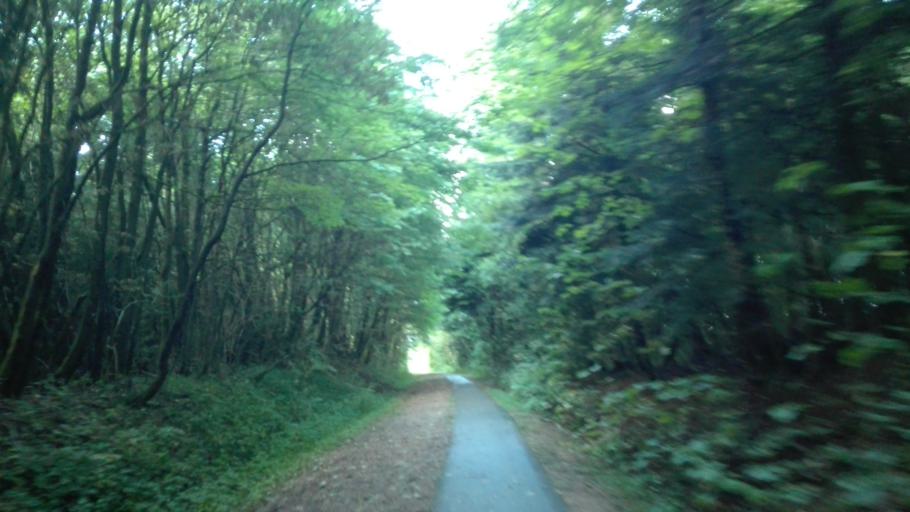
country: DK
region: Central Jutland
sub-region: Silkeborg Kommune
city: Virklund
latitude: 56.0837
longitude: 9.5305
